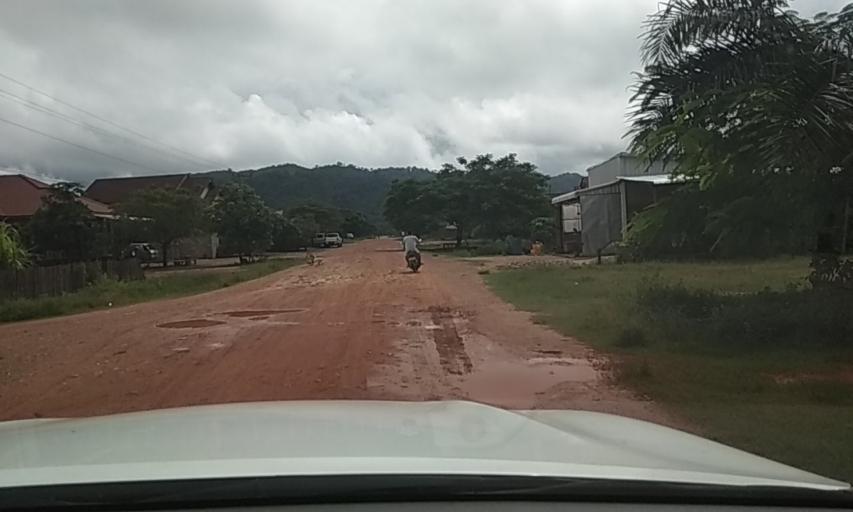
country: LA
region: Bolikhamxai
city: Bolikhan
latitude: 18.5571
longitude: 103.7347
